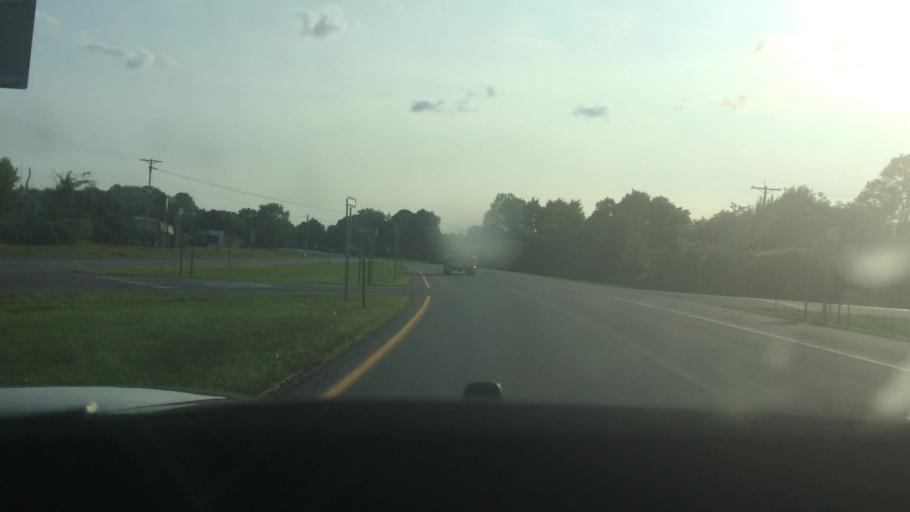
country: US
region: New York
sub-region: St. Lawrence County
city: Ogdensburg
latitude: 44.6790
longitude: -75.5194
